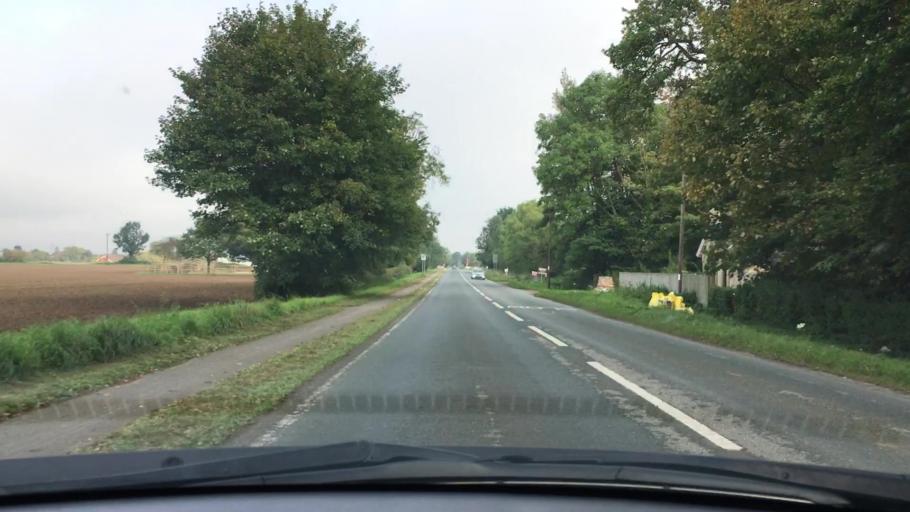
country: GB
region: England
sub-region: North East Lincolnshire
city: Waltham
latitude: 53.5122
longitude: -0.1275
